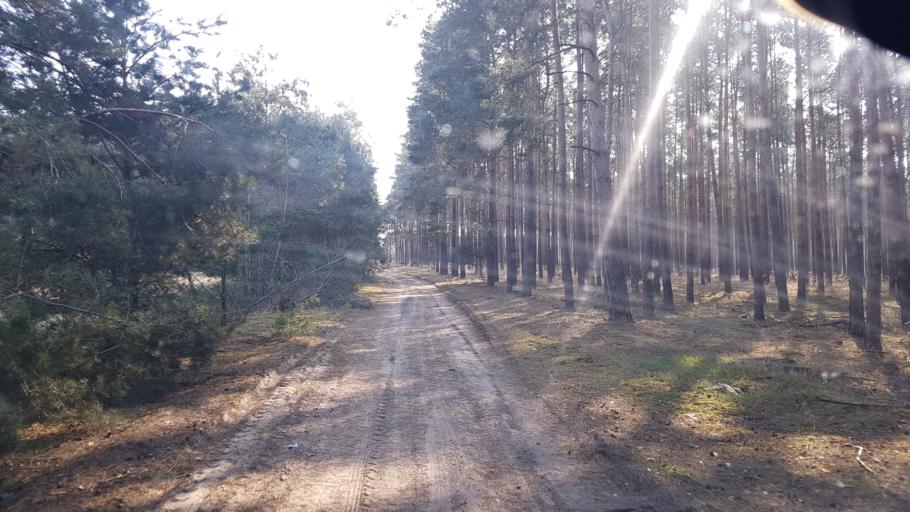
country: DE
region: Brandenburg
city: Schlieben
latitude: 51.6730
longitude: 13.3134
